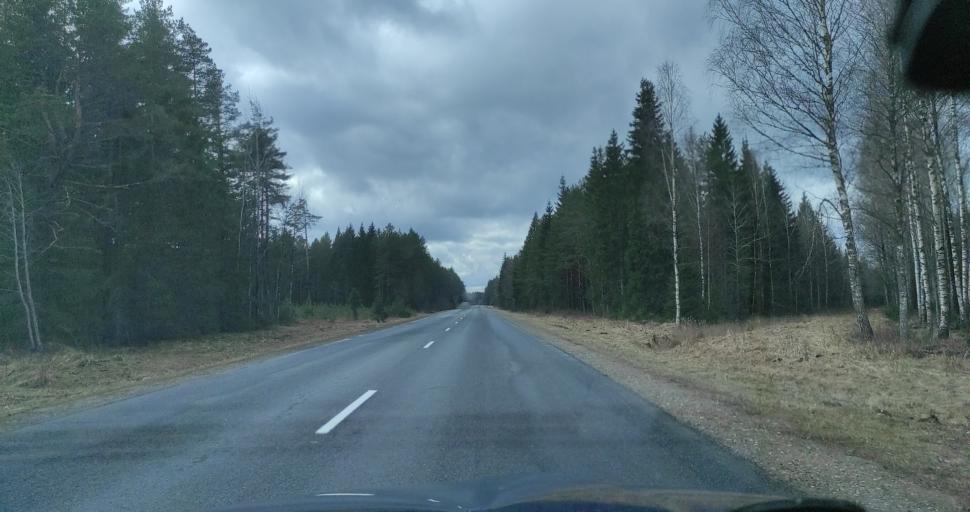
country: LV
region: Talsu Rajons
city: Stende
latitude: 57.1112
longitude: 22.5017
